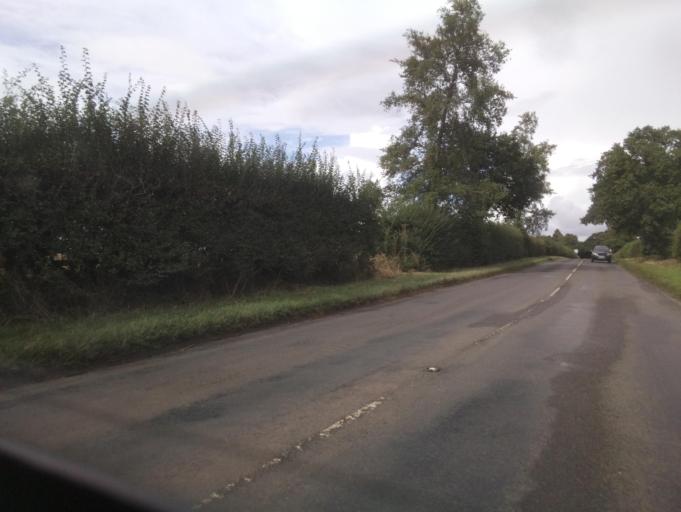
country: GB
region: England
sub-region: Shropshire
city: Shifnal
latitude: 52.6881
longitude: -2.3613
